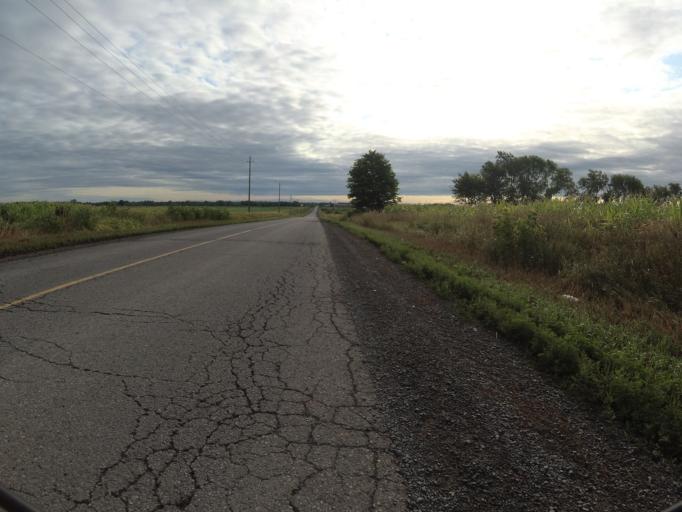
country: CA
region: Ontario
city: Clarence-Rockland
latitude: 45.3246
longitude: -75.3805
